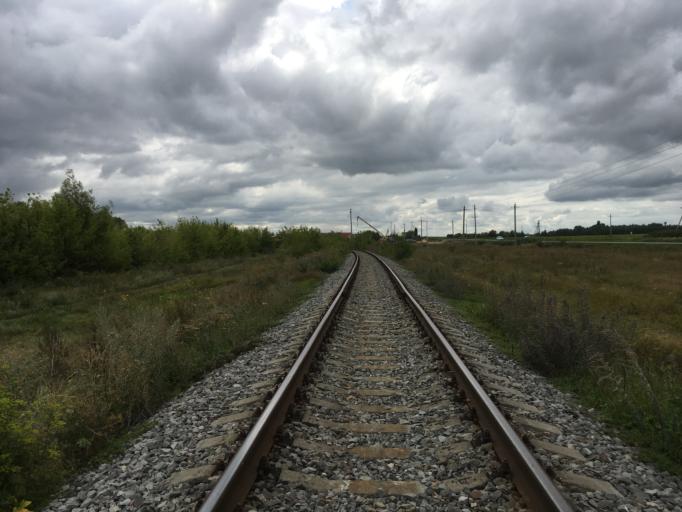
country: RU
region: Voronezj
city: Rossosh'
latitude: 50.2128
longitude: 39.5234
